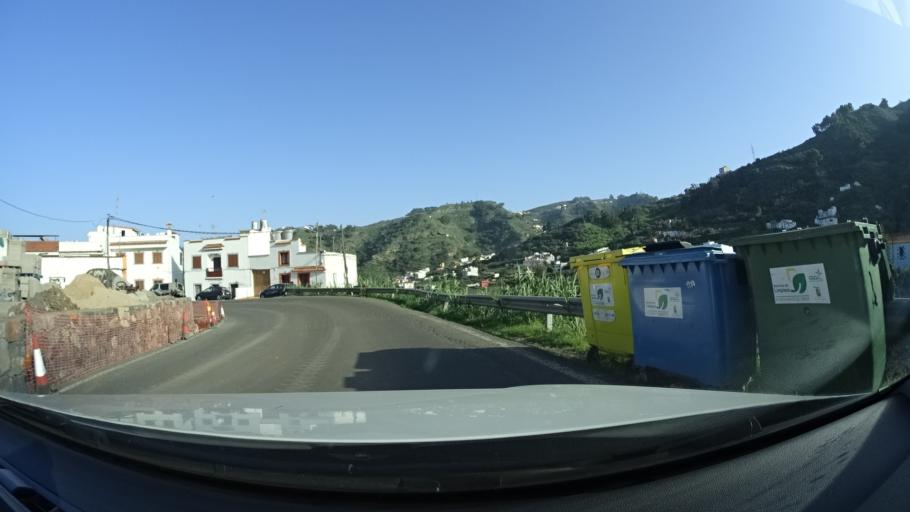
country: ES
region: Canary Islands
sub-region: Provincia de Las Palmas
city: Teror
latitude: 28.0588
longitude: -15.5507
